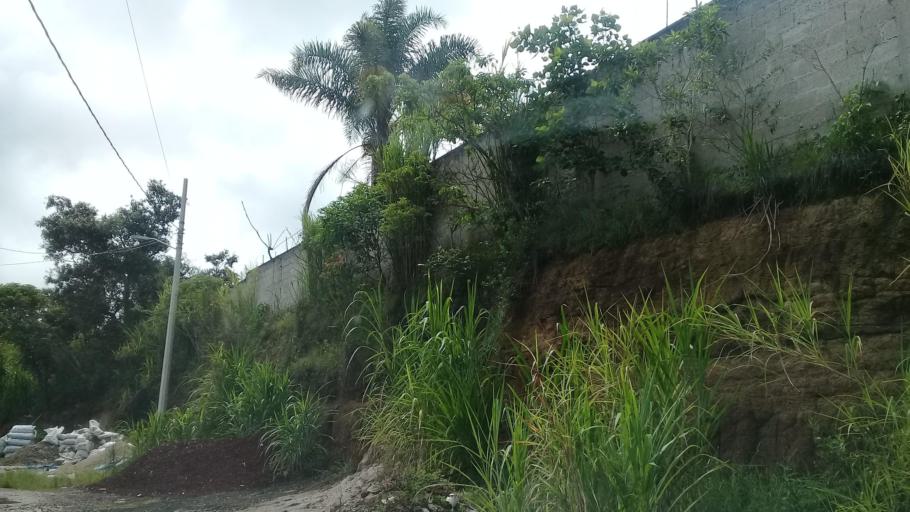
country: MX
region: Veracruz
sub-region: Emiliano Zapata
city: Jacarandas
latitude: 19.4831
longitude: -96.8554
